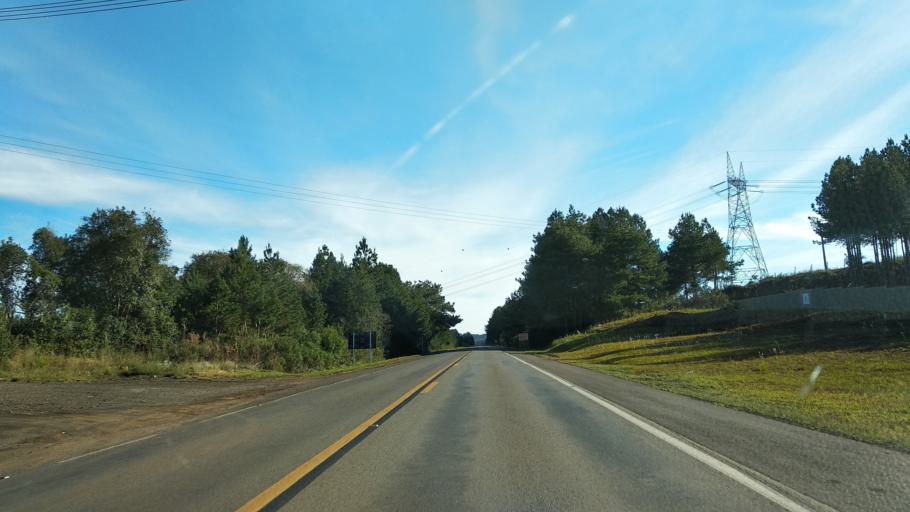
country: BR
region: Santa Catarina
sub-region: Celso Ramos
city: Celso Ramos
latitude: -27.5420
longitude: -51.4180
